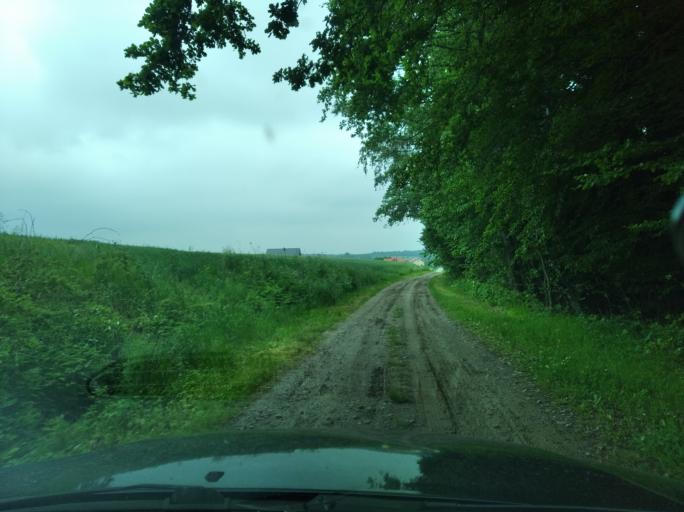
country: PL
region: Subcarpathian Voivodeship
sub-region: Powiat ropczycko-sedziszowski
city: Zagorzyce
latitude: 49.9848
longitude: 21.7058
